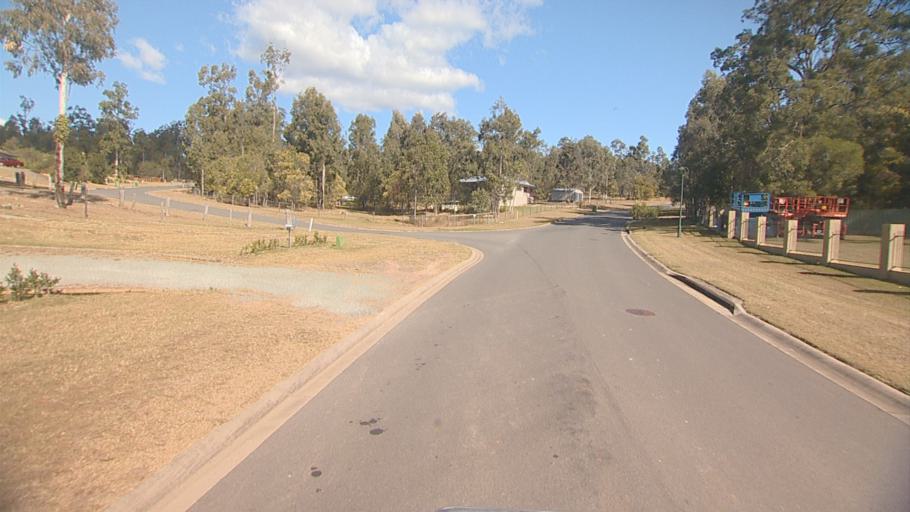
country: AU
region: Queensland
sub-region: Logan
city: North Maclean
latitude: -27.7535
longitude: 152.9403
